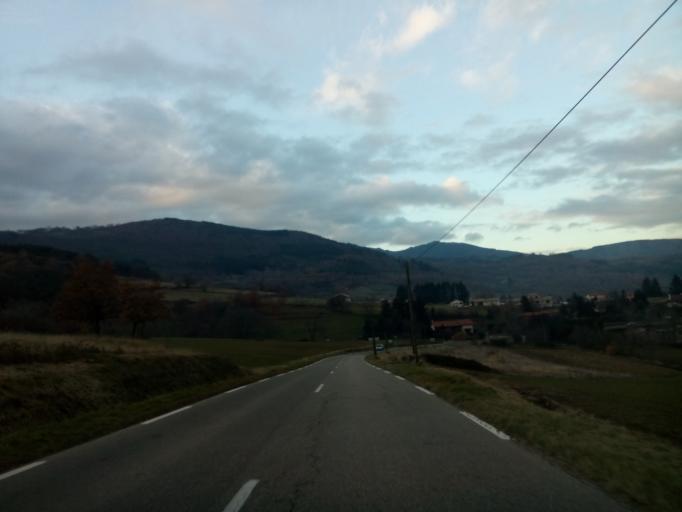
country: FR
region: Rhone-Alpes
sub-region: Departement de la Loire
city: Saint-Julien-Molin-Molette
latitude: 45.3376
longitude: 4.6473
